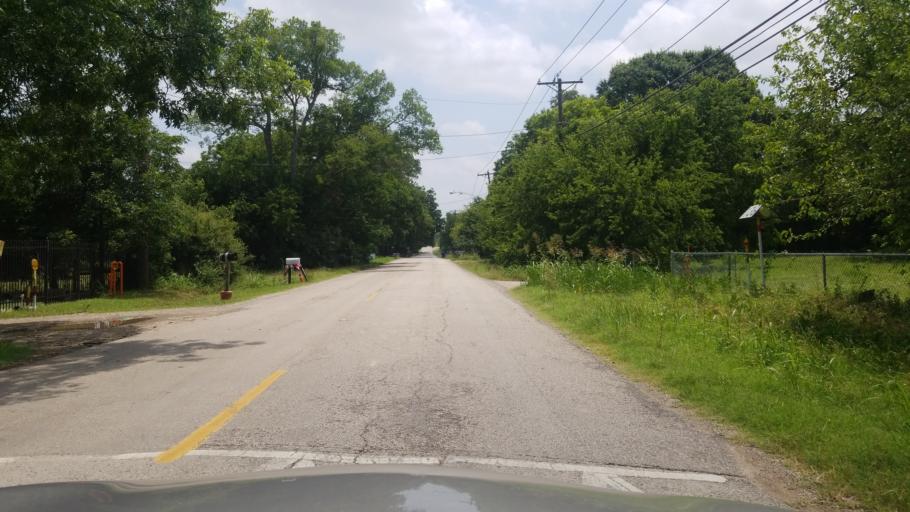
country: US
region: Texas
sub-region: Dallas County
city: Duncanville
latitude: 32.6801
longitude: -96.9138
